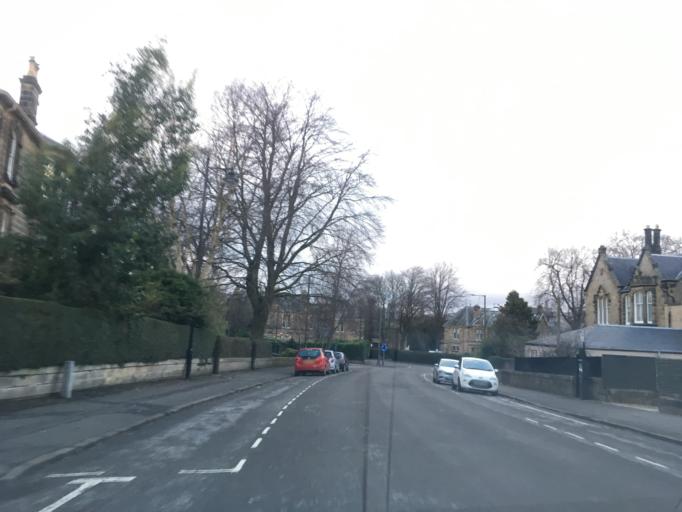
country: GB
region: Scotland
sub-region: Stirling
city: Stirling
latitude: 56.1138
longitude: -3.9414
